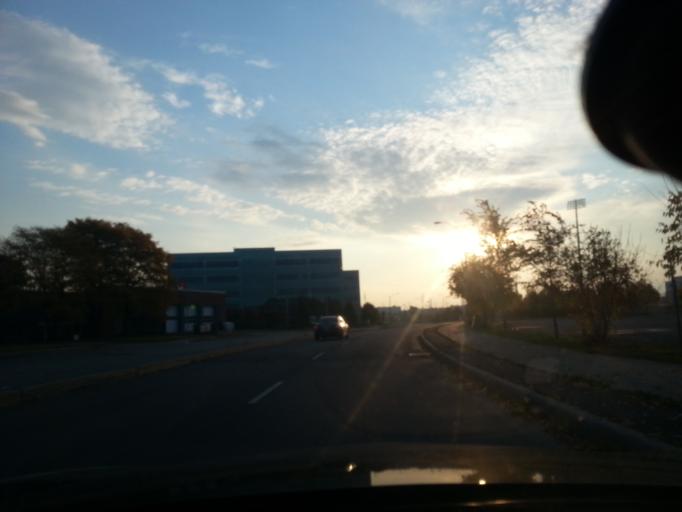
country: CA
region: Ontario
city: Ottawa
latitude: 45.4218
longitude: -75.6558
